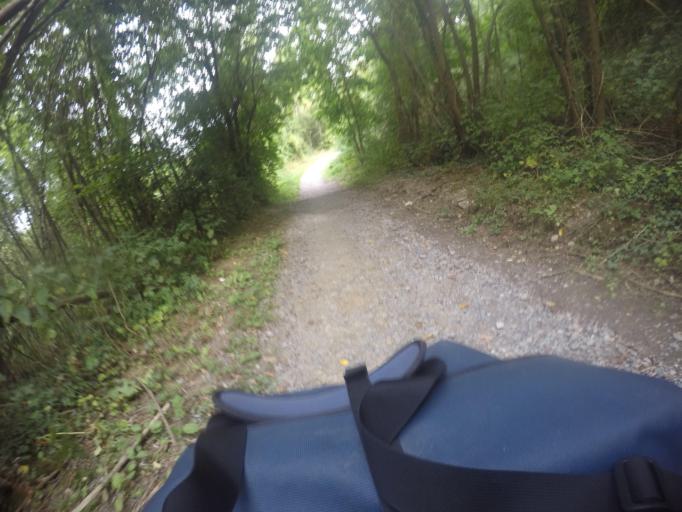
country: DE
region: North Rhine-Westphalia
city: Haan
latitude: 51.2138
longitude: 6.9983
